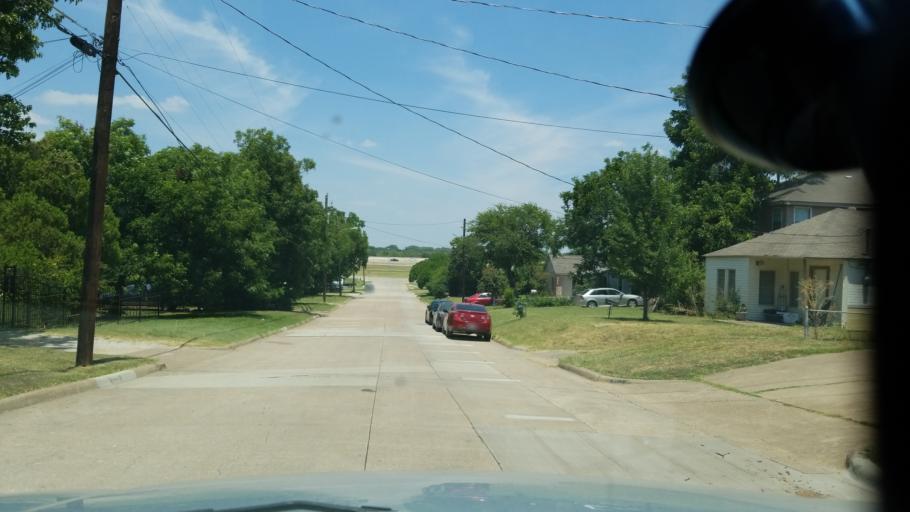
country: US
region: Texas
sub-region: Dallas County
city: Grand Prairie
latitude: 32.7584
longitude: -96.9630
